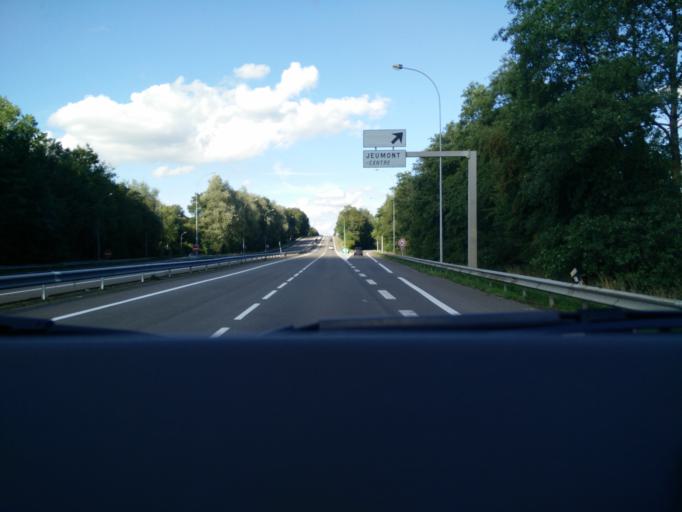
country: FR
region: Nord-Pas-de-Calais
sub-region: Departement du Nord
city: Marpent
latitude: 50.2970
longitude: 4.0788
